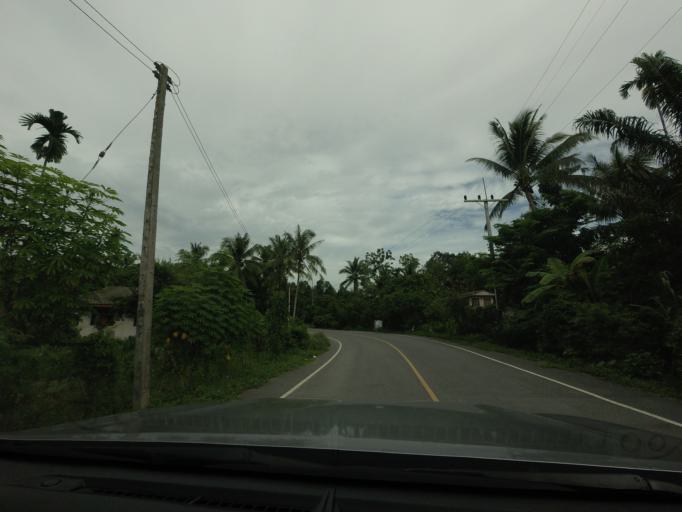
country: TH
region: Nakhon Si Thammarat
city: Phra Phrom
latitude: 8.2834
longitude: 99.9320
